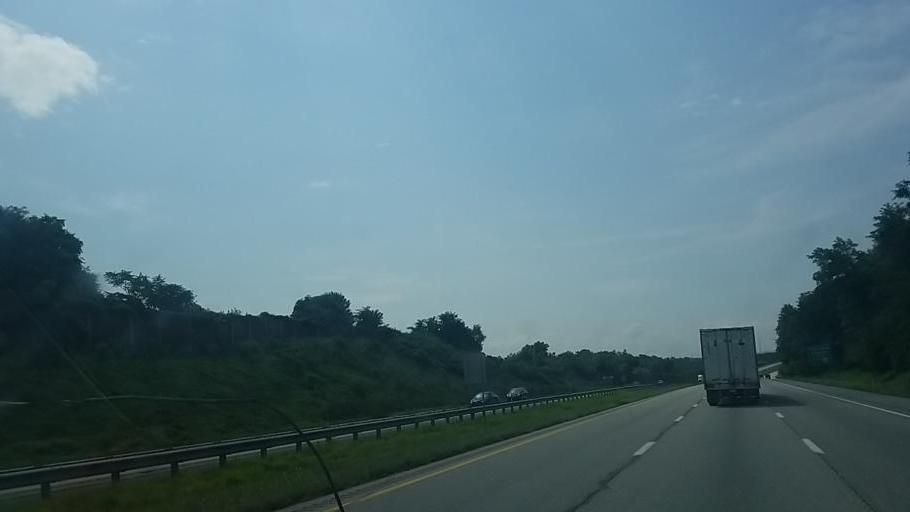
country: US
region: Pennsylvania
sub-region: Dauphin County
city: Harrisburg
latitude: 40.3128
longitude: -76.8817
